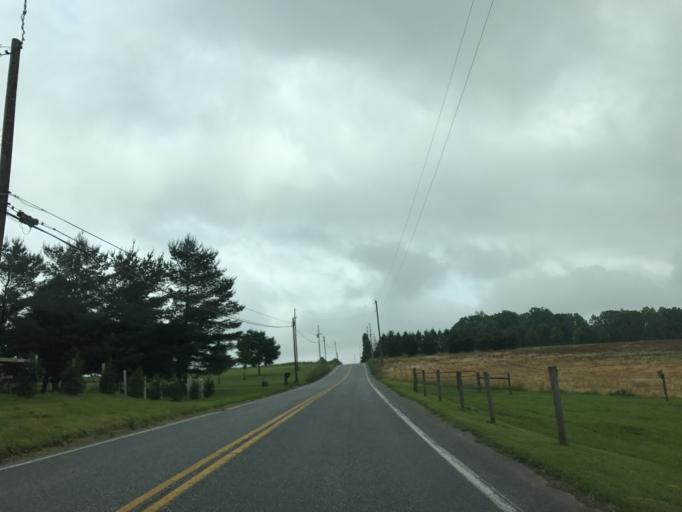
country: US
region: Pennsylvania
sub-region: York County
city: Stewartstown
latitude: 39.8194
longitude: -76.6060
